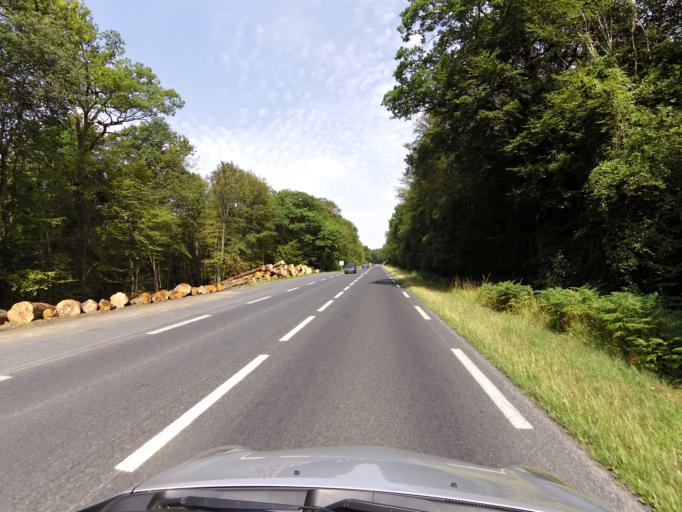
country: FR
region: Champagne-Ardenne
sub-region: Departement de la Marne
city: Rilly-la-Montagne
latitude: 49.1502
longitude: 4.0092
